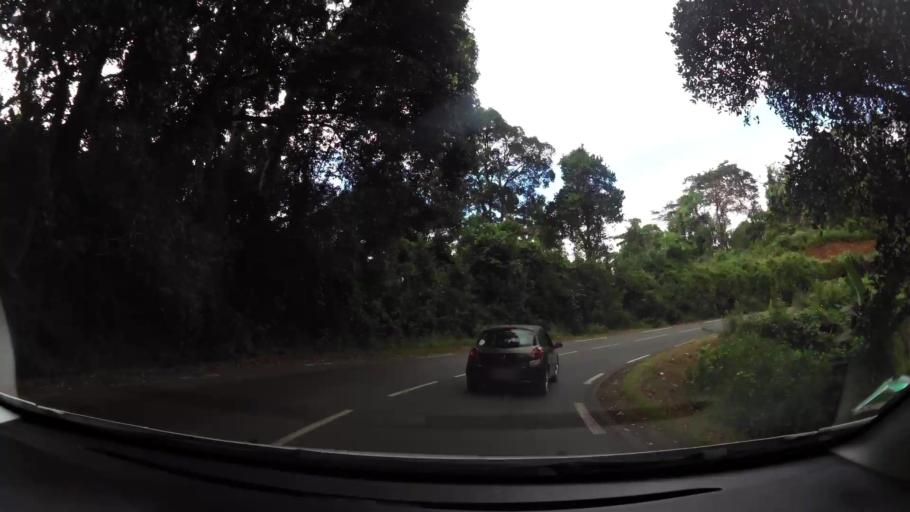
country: YT
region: Dembeni
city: Dembeni
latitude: -12.8411
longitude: 45.1669
